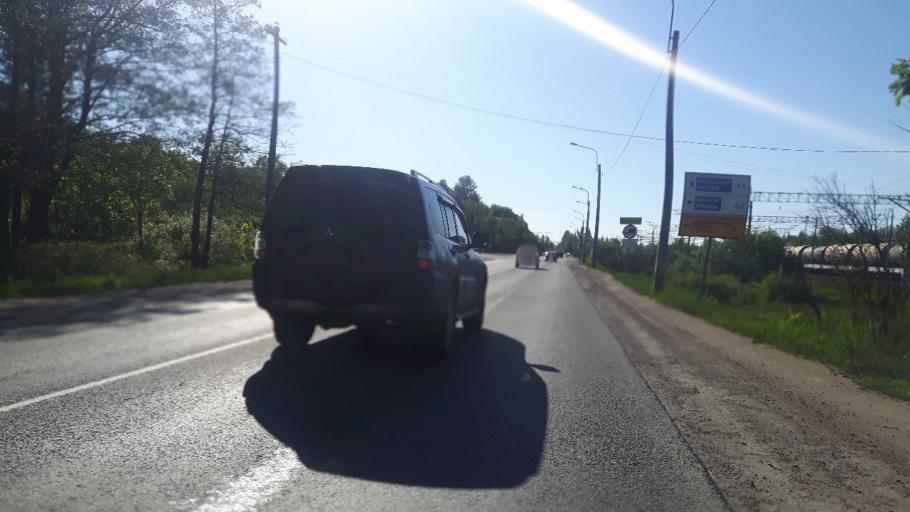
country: RU
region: St.-Petersburg
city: Bol'shaya Izhora
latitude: 59.9272
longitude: 29.6593
